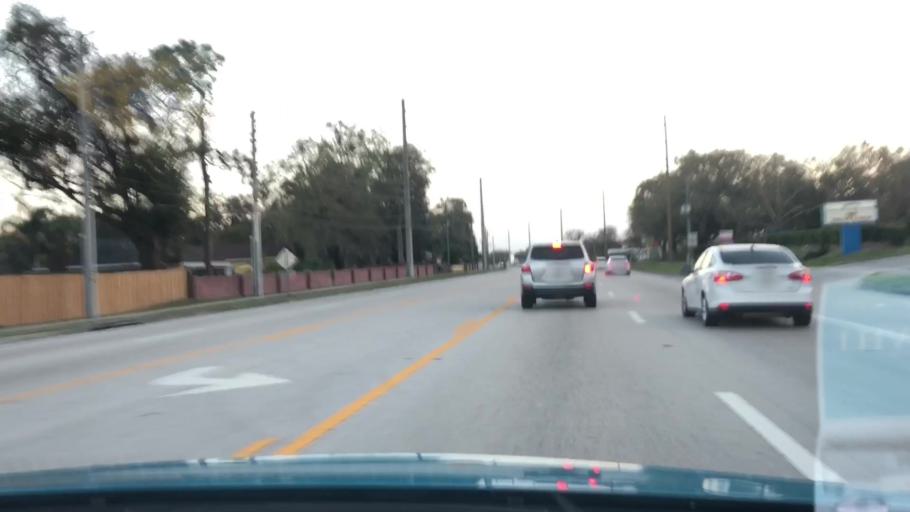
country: US
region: Florida
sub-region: Osceola County
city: Buenaventura Lakes
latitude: 28.3333
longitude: -81.3904
